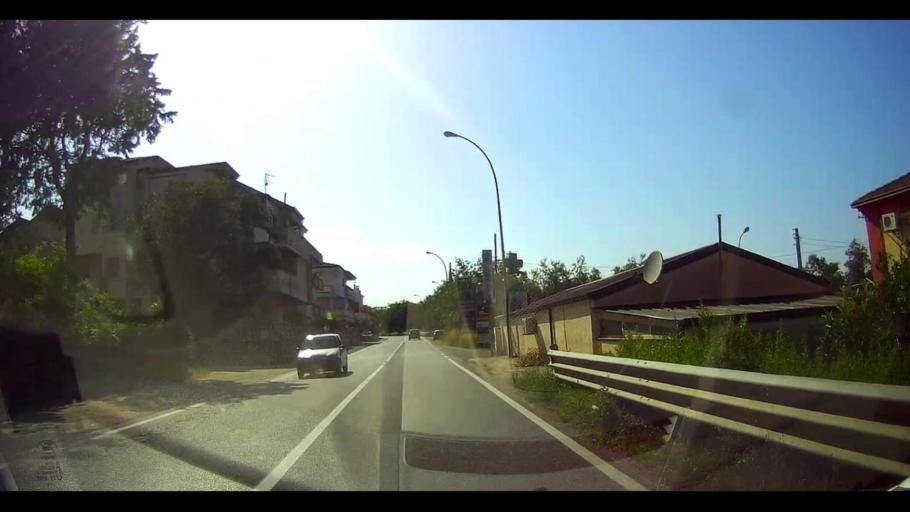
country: IT
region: Calabria
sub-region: Provincia di Cosenza
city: Cariati
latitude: 39.4838
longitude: 16.9742
